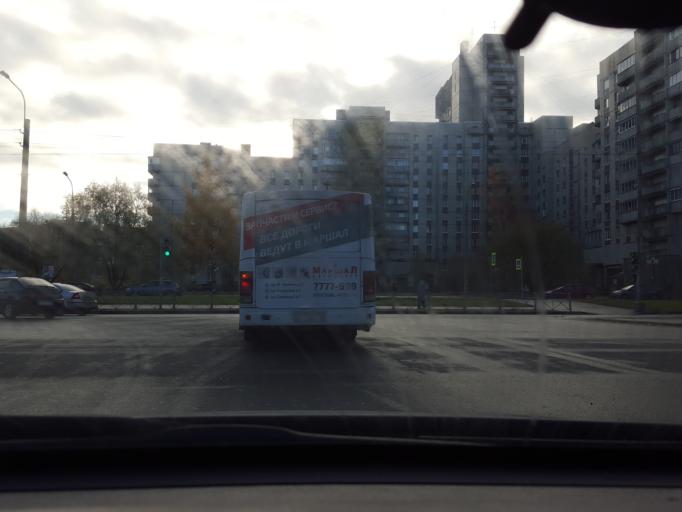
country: RU
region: St.-Petersburg
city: Ozerki
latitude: 60.0446
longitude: 30.3201
